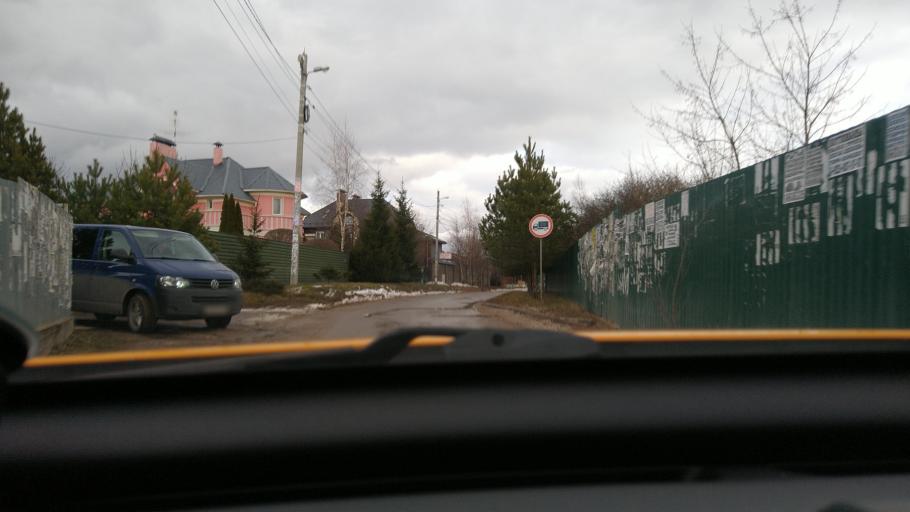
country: RU
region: Moskovskaya
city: Petrovo-Dal'neye
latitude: 55.7704
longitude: 37.1989
